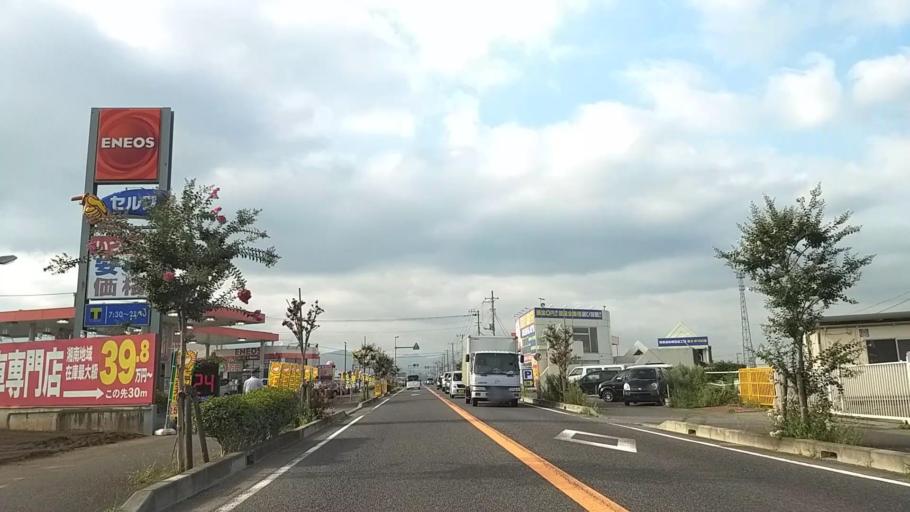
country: JP
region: Kanagawa
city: Isehara
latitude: 35.3609
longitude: 139.3252
